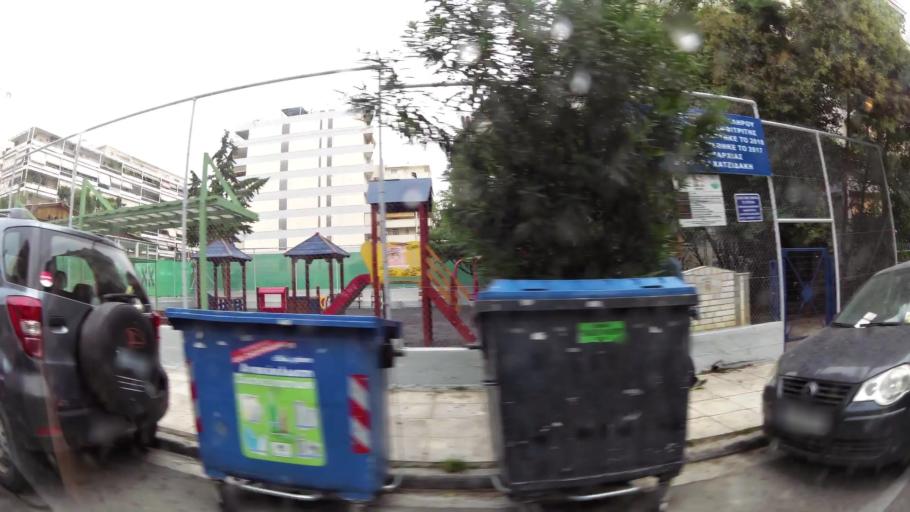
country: GR
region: Attica
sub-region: Nomarchia Athinas
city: Palaio Faliro
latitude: 37.9226
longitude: 23.6996
